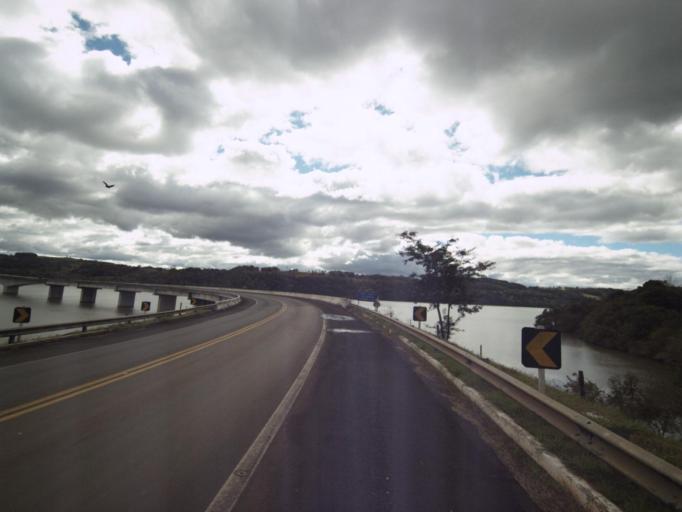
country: BR
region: Santa Catarina
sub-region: Concordia
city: Concordia
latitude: -27.3795
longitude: -51.9852
